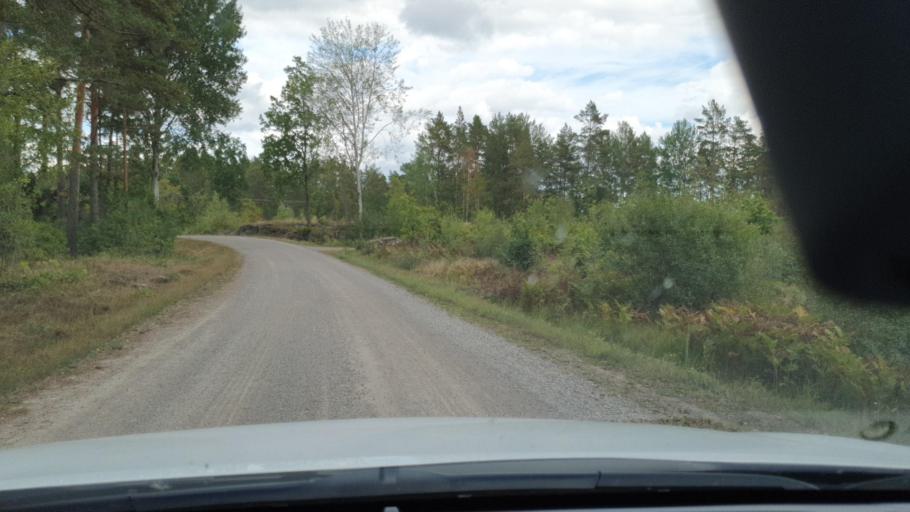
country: SE
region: Kalmar
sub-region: Vasterviks Kommun
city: Vaestervik
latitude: 57.7259
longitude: 16.4793
